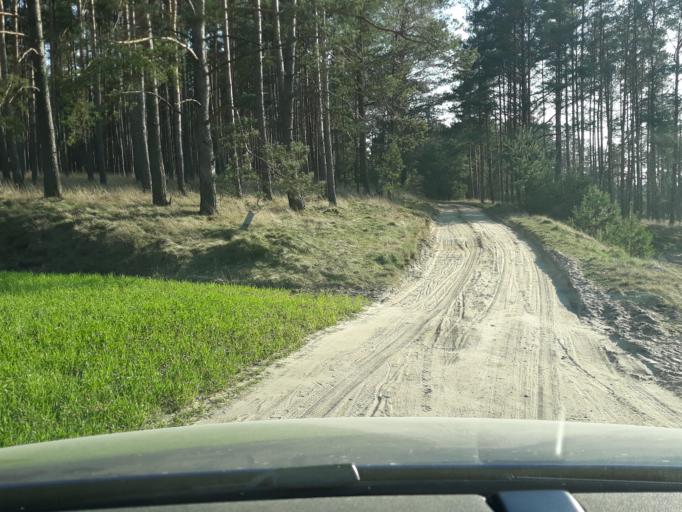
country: PL
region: Pomeranian Voivodeship
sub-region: Powiat bytowski
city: Lipnica
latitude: 53.8916
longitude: 17.4934
